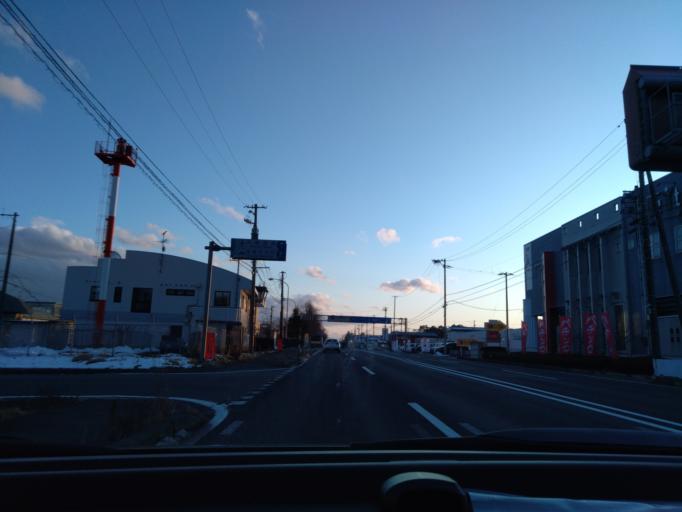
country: JP
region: Iwate
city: Hanamaki
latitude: 39.4304
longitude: 141.1316
